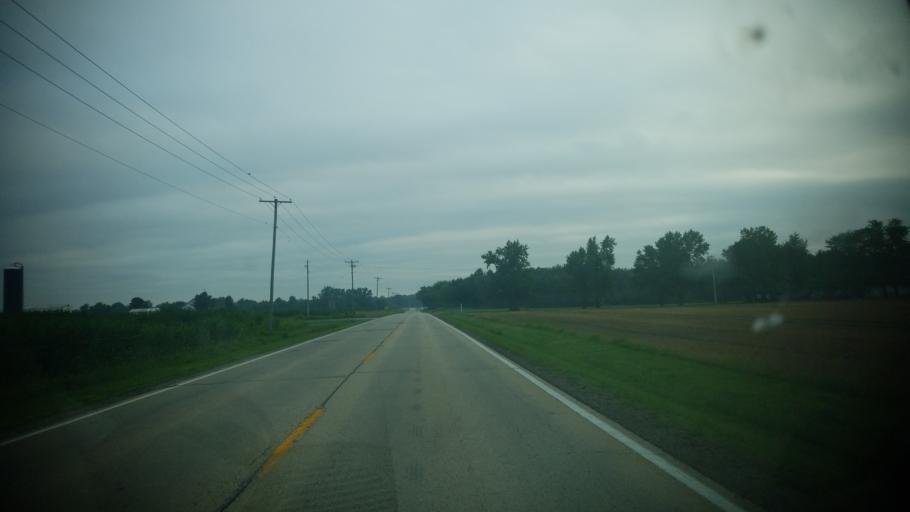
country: US
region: Illinois
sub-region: Clay County
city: Flora
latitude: 38.6638
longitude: -88.4383
